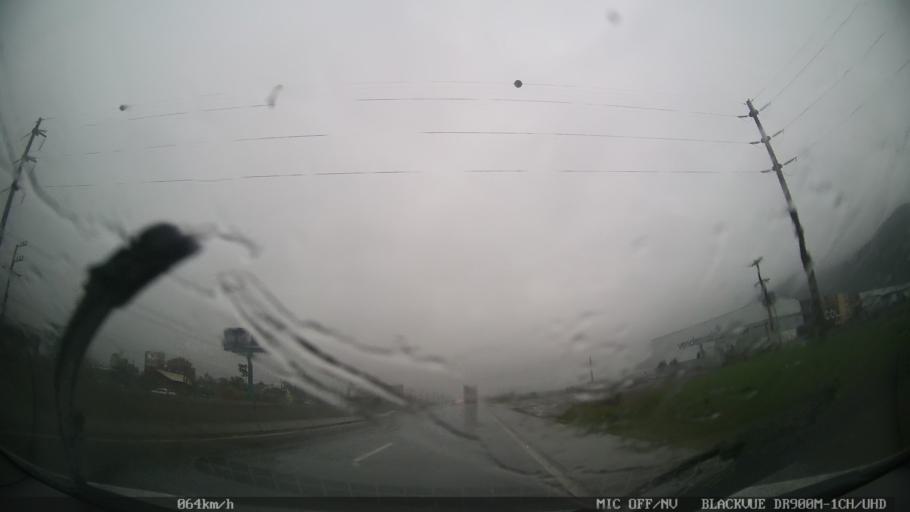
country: BR
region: Santa Catarina
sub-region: Navegantes
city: Navegantes
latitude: -26.8560
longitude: -48.6986
